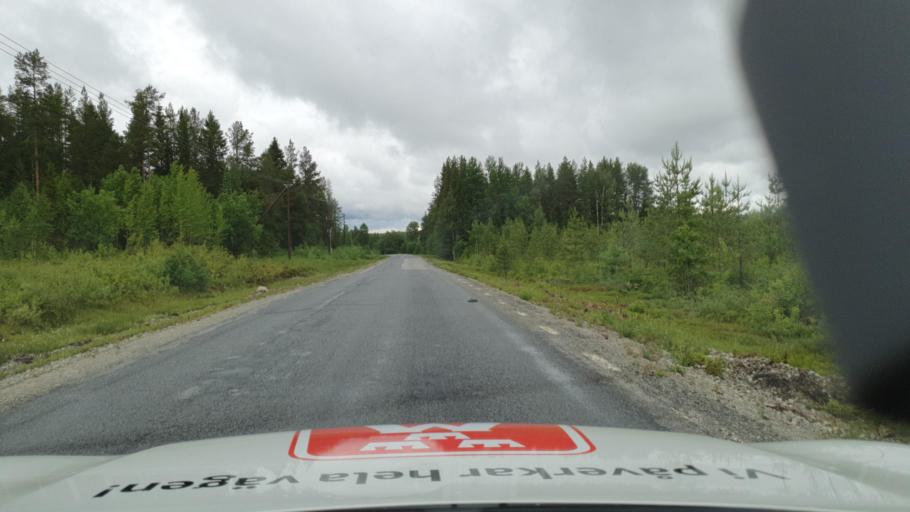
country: SE
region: Vaesterbotten
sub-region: Dorotea Kommun
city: Dorotea
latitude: 64.1708
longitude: 16.6490
